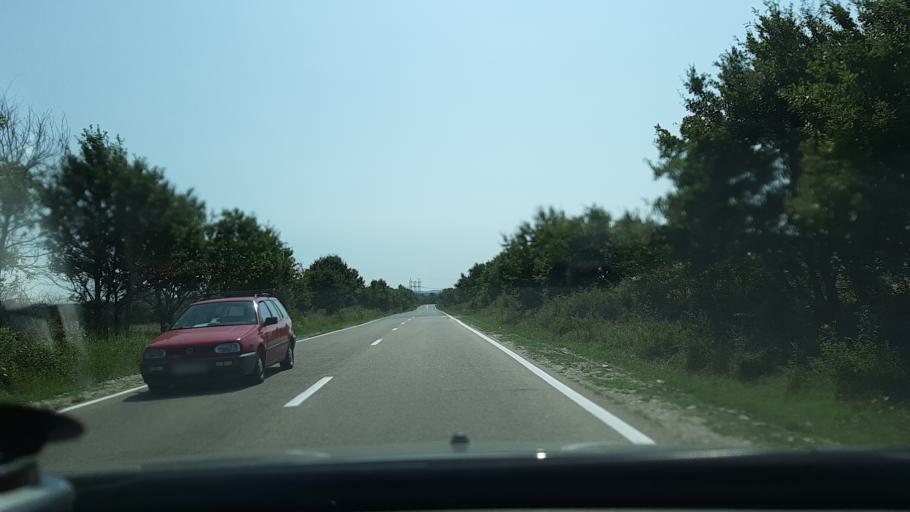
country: RO
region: Gorj
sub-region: Comuna Targu Carbunesti
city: Pojogeni
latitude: 45.0044
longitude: 23.4861
